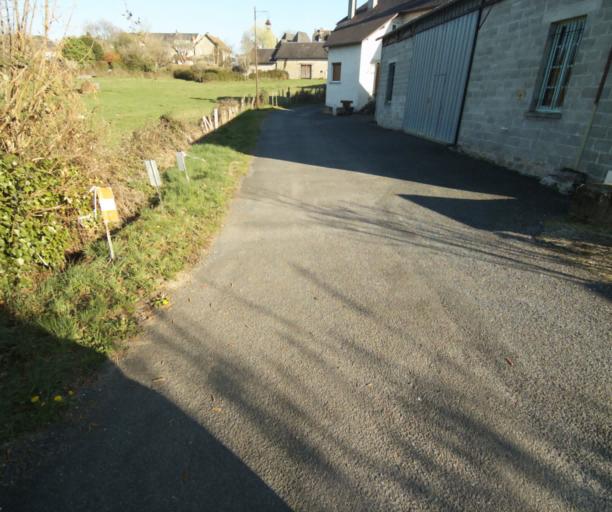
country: FR
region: Limousin
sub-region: Departement de la Correze
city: Chamboulive
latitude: 45.4653
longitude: 1.7277
